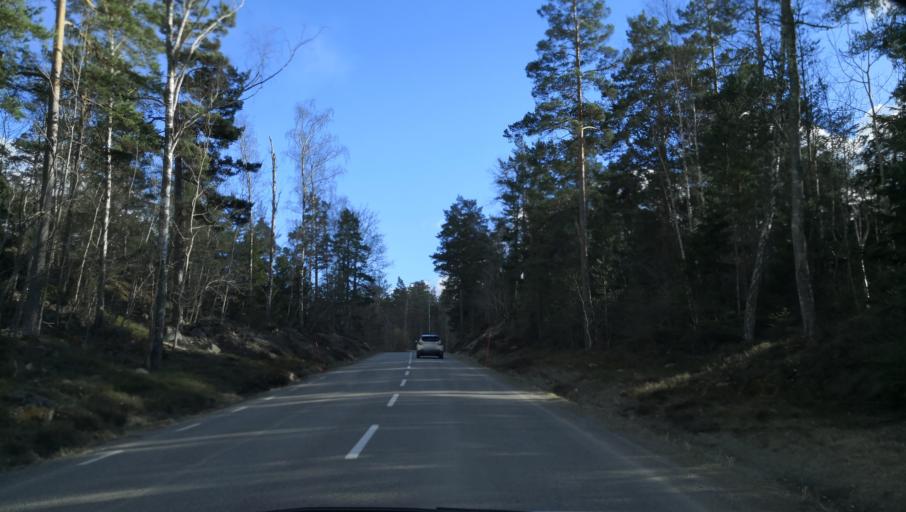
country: SE
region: Stockholm
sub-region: Varmdo Kommun
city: Mortnas
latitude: 59.2841
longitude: 18.4546
